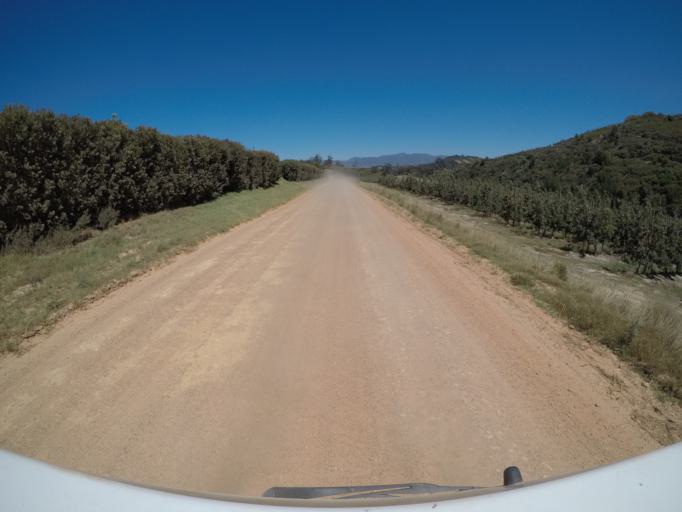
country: ZA
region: Western Cape
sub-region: Overberg District Municipality
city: Grabouw
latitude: -34.2449
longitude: 19.1039
